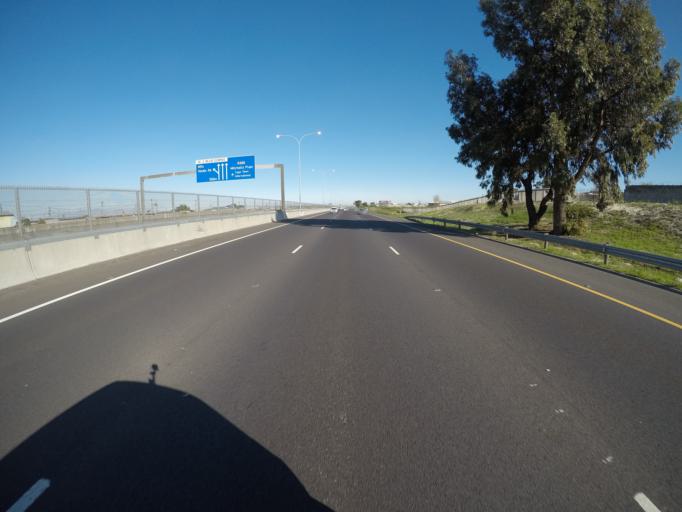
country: ZA
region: Western Cape
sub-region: City of Cape Town
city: Kraaifontein
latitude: -33.9695
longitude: 18.6542
